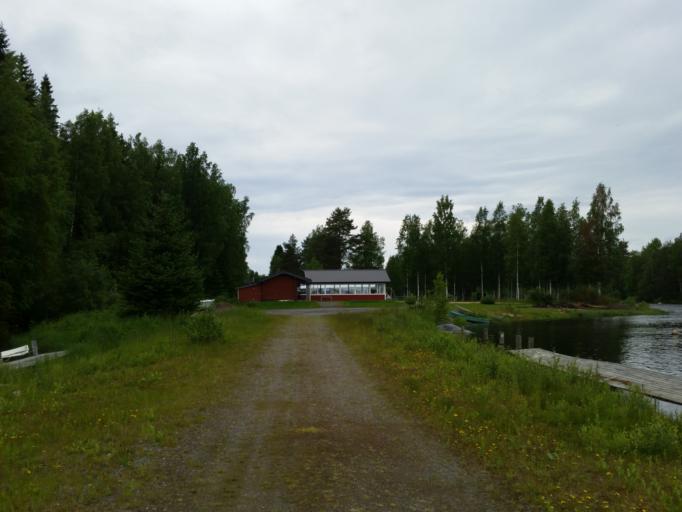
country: FI
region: Northern Savo
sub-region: Sisae-Savo
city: Tervo
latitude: 63.0051
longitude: 26.6906
